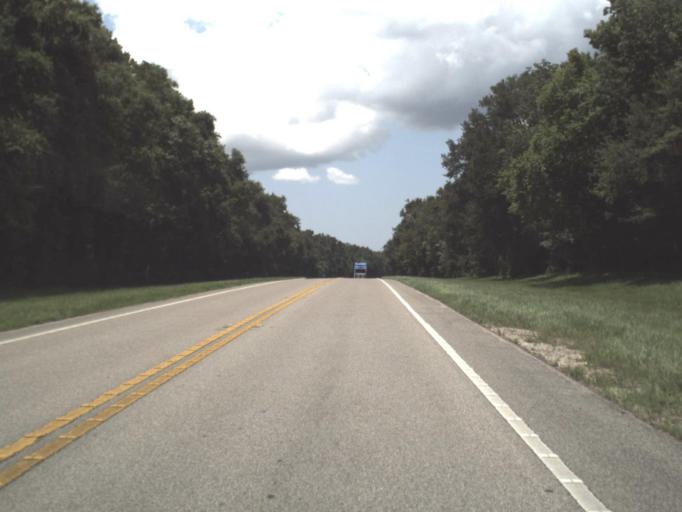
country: US
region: Florida
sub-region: Hernando County
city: North Brooksville
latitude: 28.6432
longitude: -82.4356
